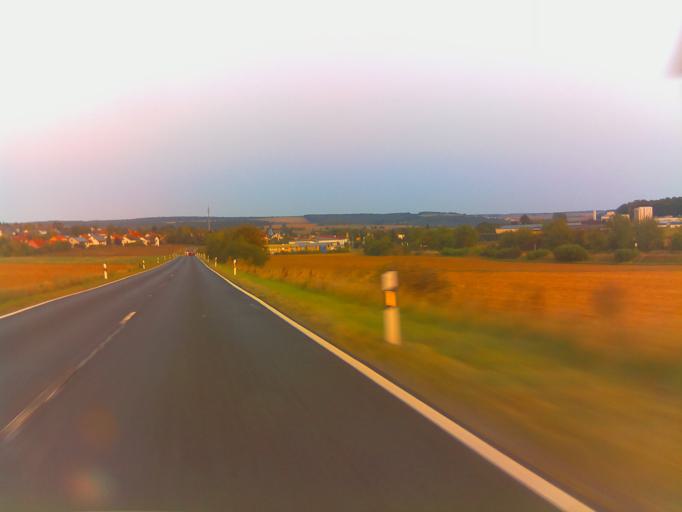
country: DE
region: Bavaria
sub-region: Regierungsbezirk Unterfranken
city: Oerlenbach
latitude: 50.1494
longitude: 10.1172
